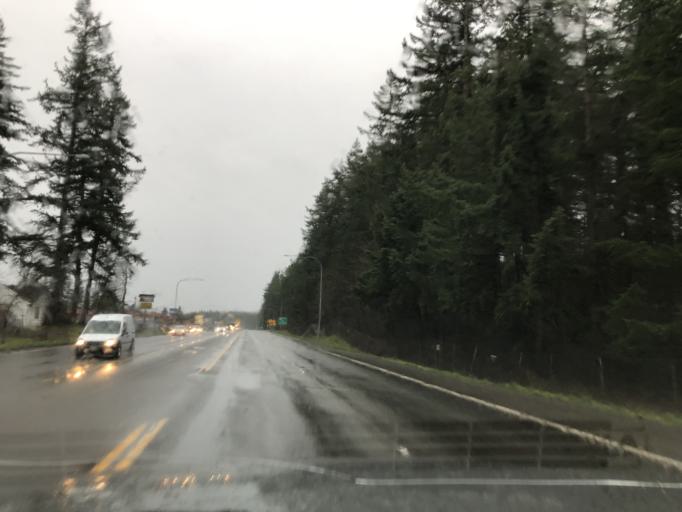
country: US
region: Washington
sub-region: Pierce County
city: Spanaway
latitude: 47.0920
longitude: -122.4351
